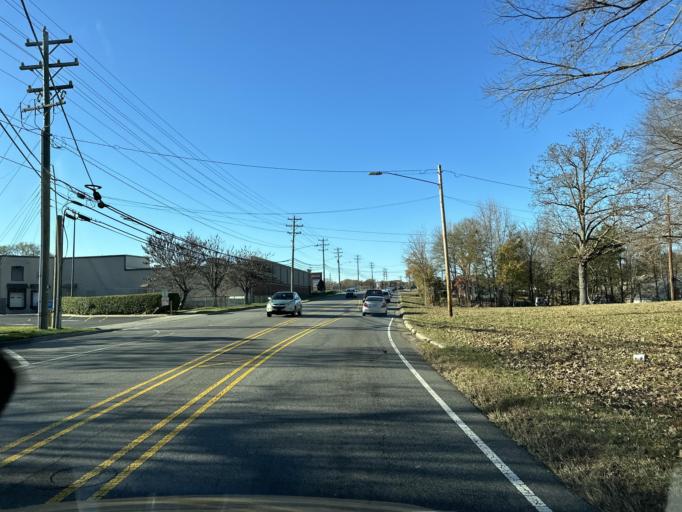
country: US
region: North Carolina
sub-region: Gaston County
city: Mount Holly
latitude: 35.3188
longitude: -80.9501
